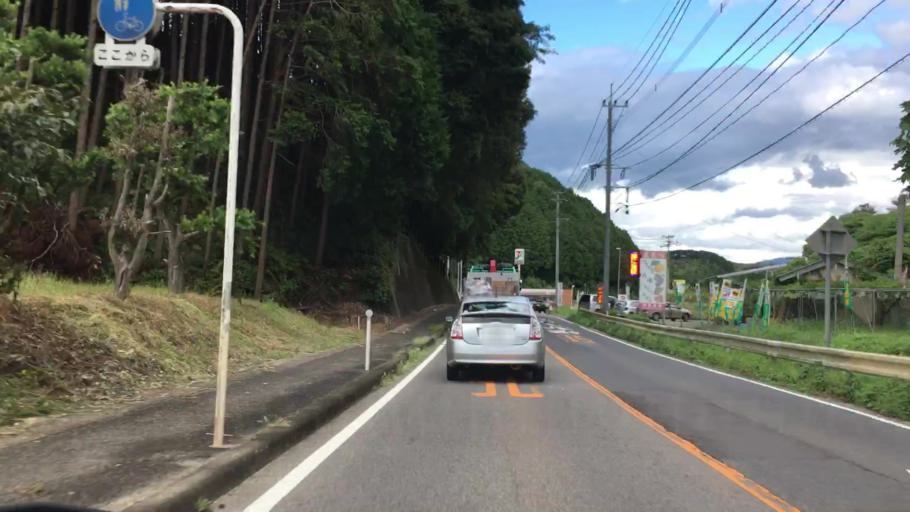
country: JP
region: Saga Prefecture
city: Imaricho-ko
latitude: 33.2920
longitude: 129.9092
